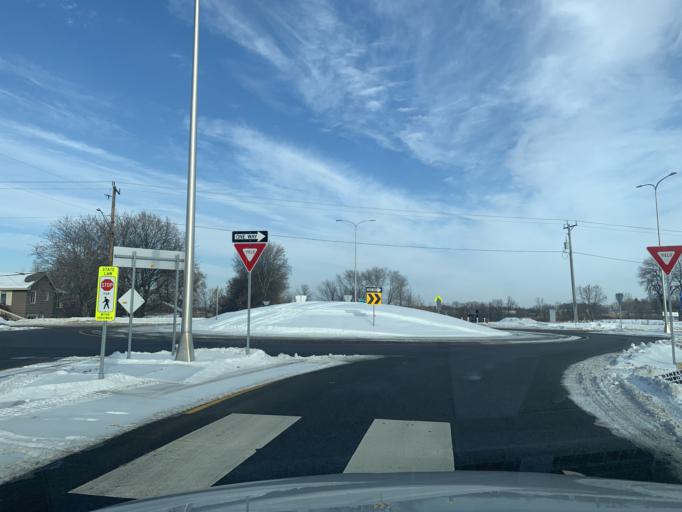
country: US
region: Minnesota
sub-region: Wright County
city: Albertville
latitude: 45.2239
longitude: -93.6440
